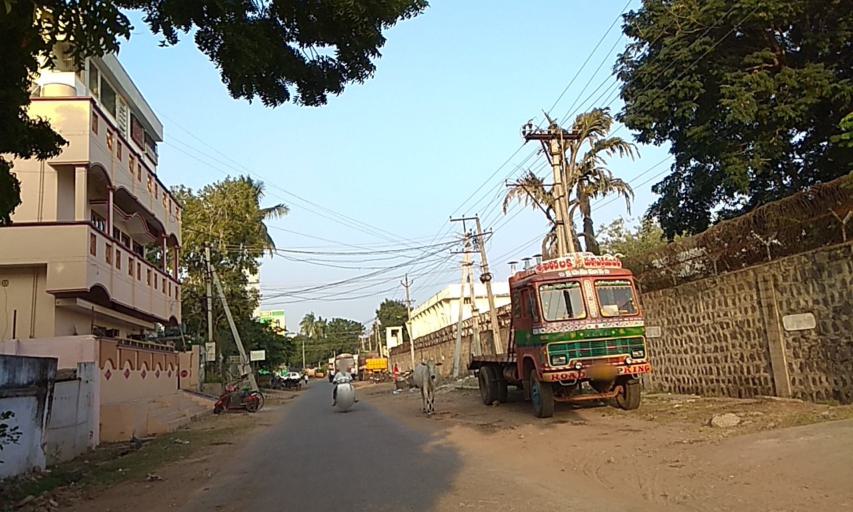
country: IN
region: Andhra Pradesh
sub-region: Krishna
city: Machilipatnam
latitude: 16.1880
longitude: 81.1349
